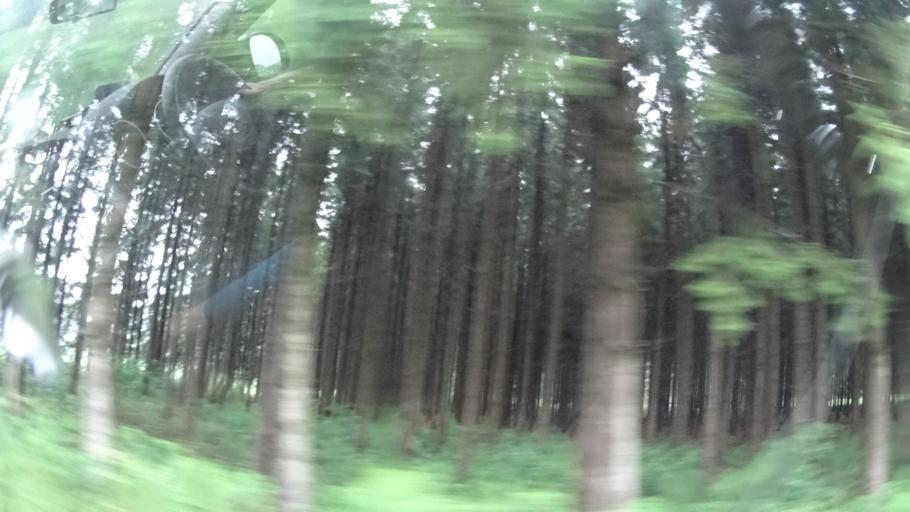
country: BE
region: Wallonia
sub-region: Province de Namur
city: Bievre
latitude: 49.9532
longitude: 5.0461
